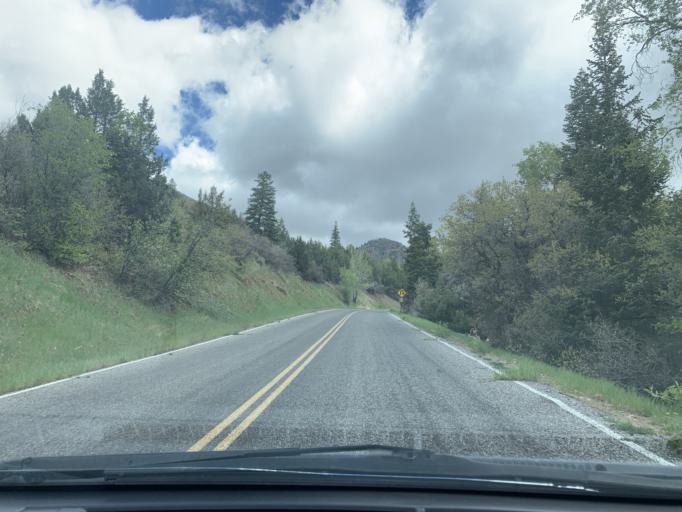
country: US
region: Utah
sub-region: Juab County
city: Nephi
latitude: 39.7804
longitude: -111.6928
